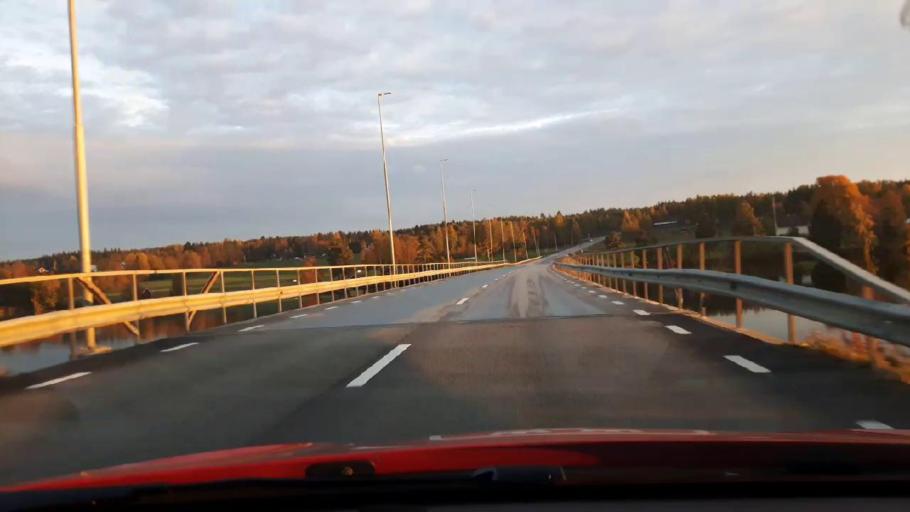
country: SE
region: Jaemtland
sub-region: OEstersunds Kommun
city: Lit
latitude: 63.3131
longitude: 14.8689
